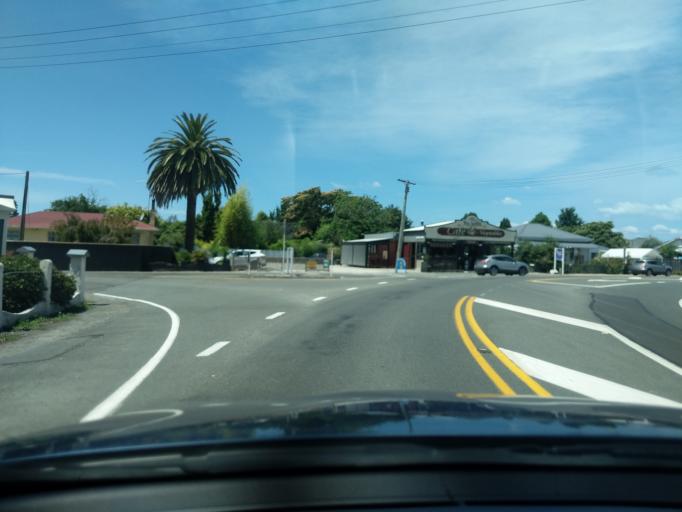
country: NZ
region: Tasman
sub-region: Tasman District
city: Motueka
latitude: -41.0763
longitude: 172.9970
